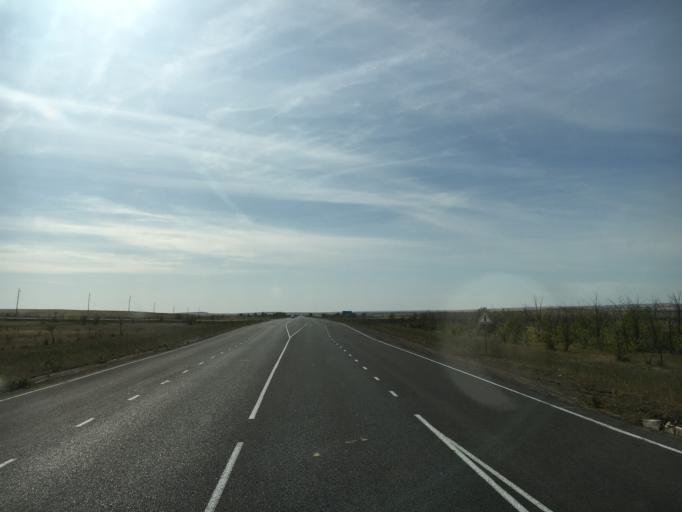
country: KZ
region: Batys Qazaqstan
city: Kamenka
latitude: 51.1133
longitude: 50.4964
